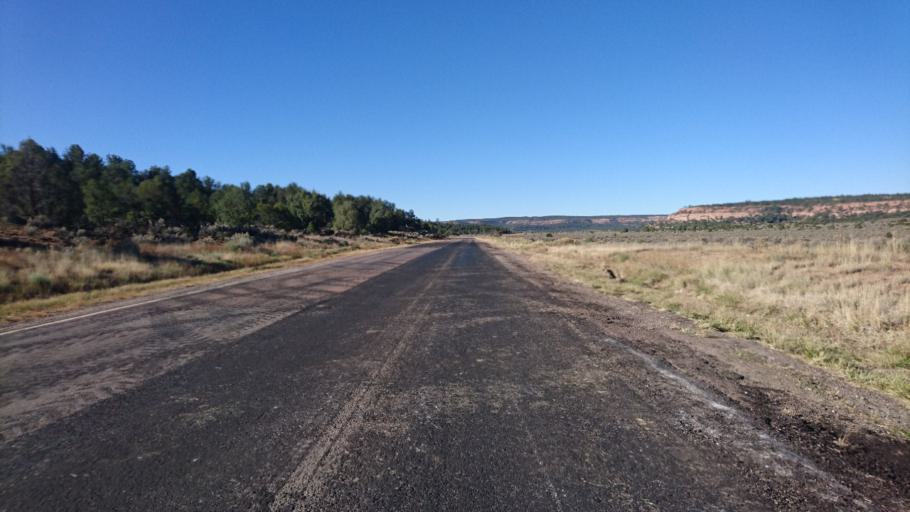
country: US
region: New Mexico
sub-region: McKinley County
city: Black Rock
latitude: 35.1163
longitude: -108.5517
